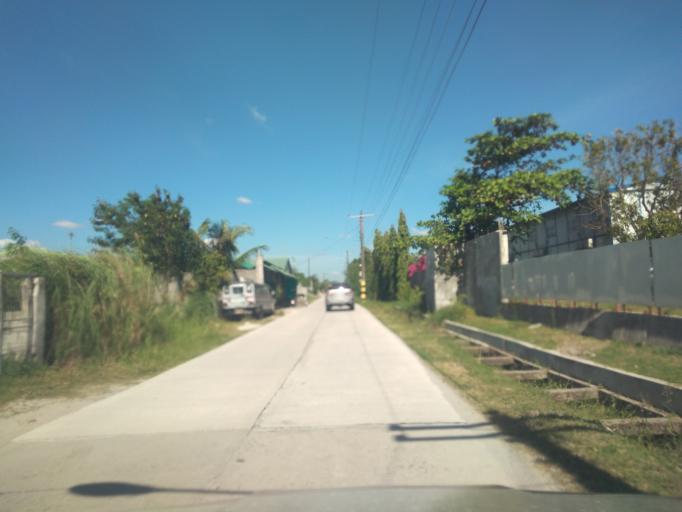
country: PH
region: Central Luzon
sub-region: Province of Pampanga
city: Bacolor
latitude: 15.0229
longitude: 120.6380
